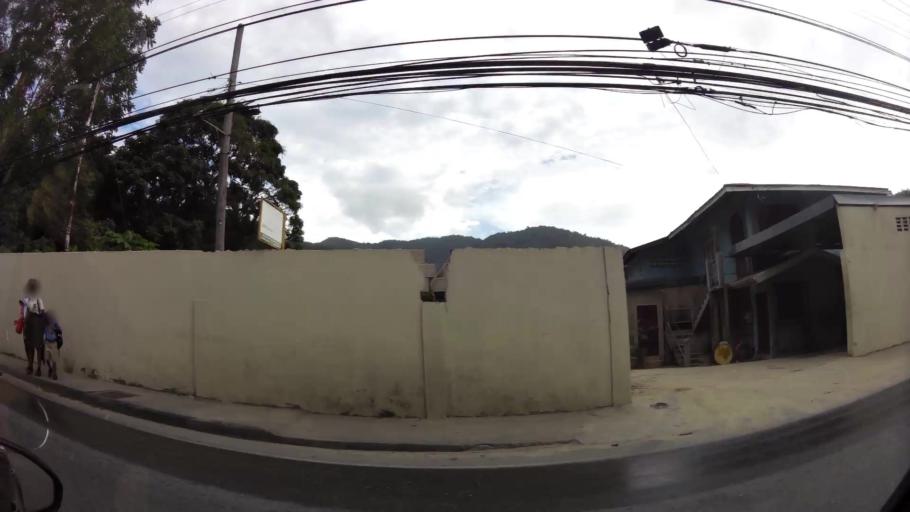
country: TT
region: San Juan/Laventille
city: Laventille
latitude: 10.6735
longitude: -61.4498
